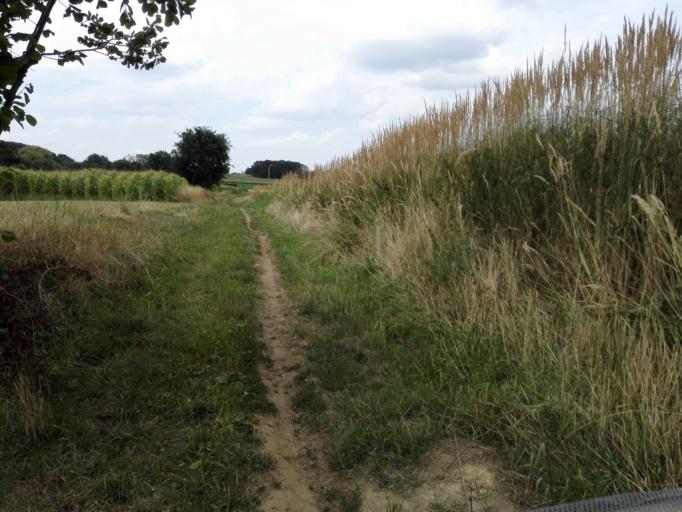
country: BE
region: Flanders
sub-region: Provincie Vlaams-Brabant
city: Holsbeek
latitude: 50.9018
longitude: 4.7887
